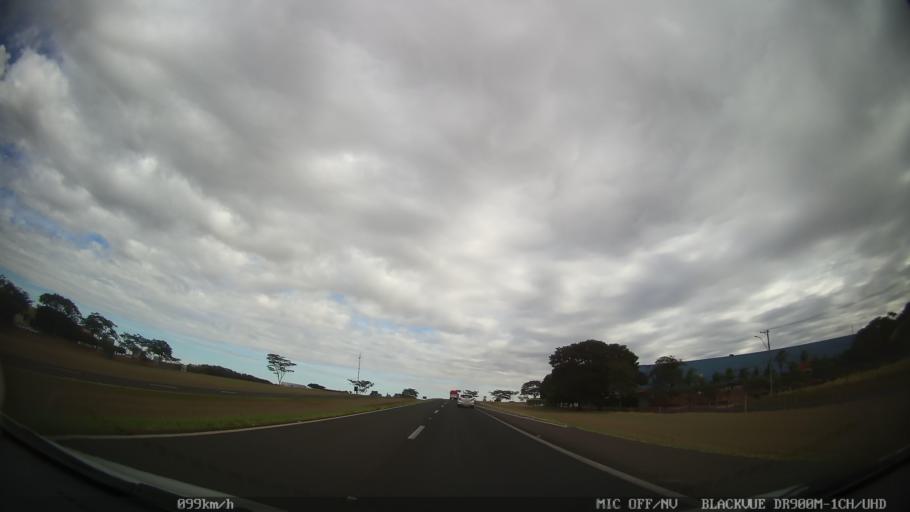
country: BR
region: Sao Paulo
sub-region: Bady Bassitt
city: Bady Bassitt
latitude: -20.8051
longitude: -49.5220
